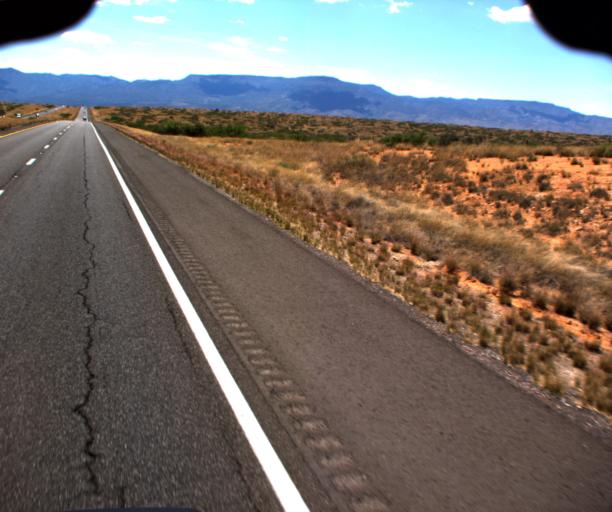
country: US
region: Arizona
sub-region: Yavapai County
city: Cornville
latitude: 34.7690
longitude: -111.9384
